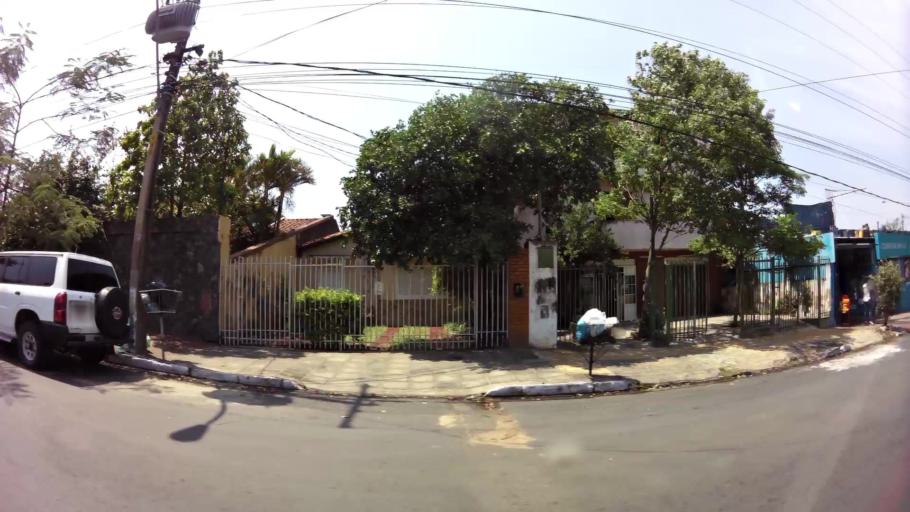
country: PY
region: Asuncion
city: Asuncion
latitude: -25.2962
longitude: -57.6539
